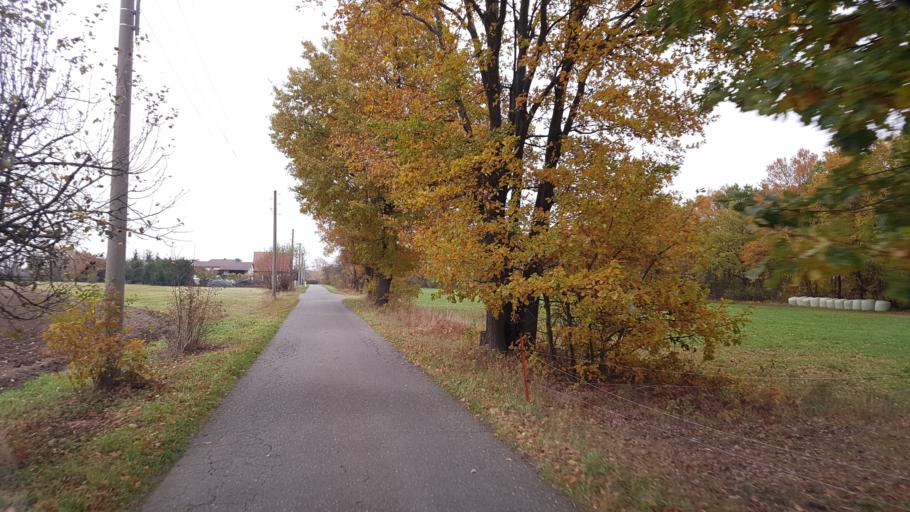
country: DE
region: Brandenburg
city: Finsterwalde
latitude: 51.6749
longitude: 13.7122
